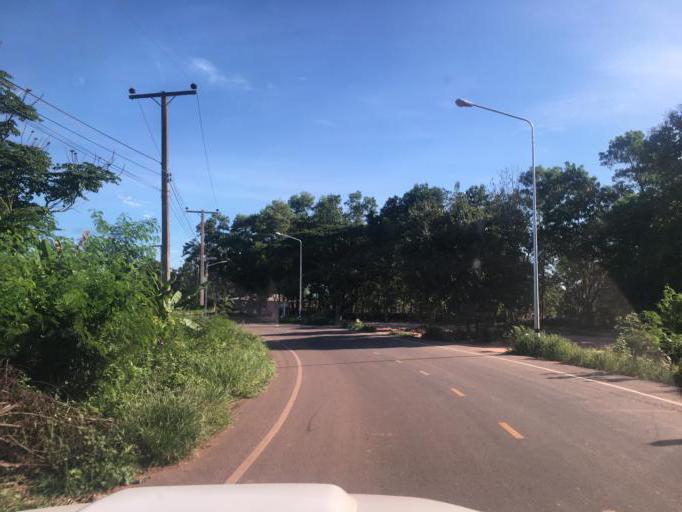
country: TH
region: Changwat Udon Thani
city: Kut Chap
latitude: 17.5222
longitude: 102.5966
